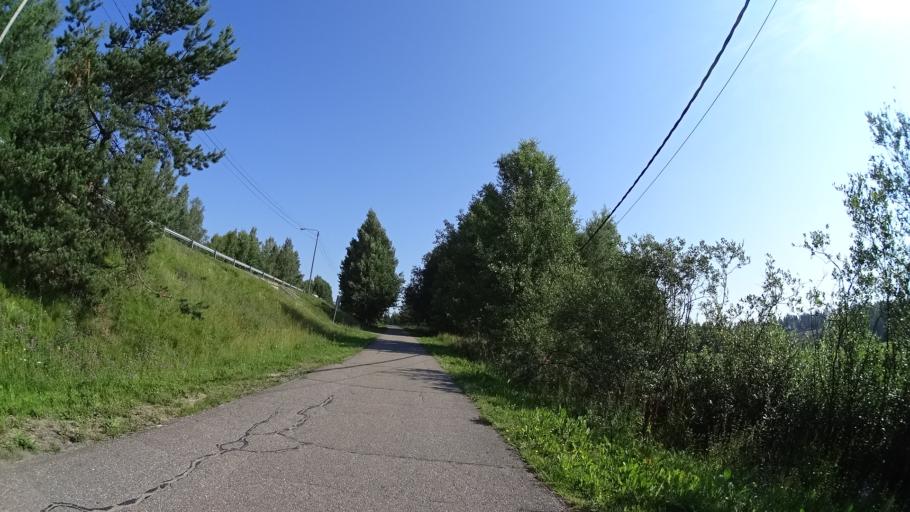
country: FI
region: Uusimaa
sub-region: Helsinki
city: Kerava
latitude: 60.3299
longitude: 25.1234
